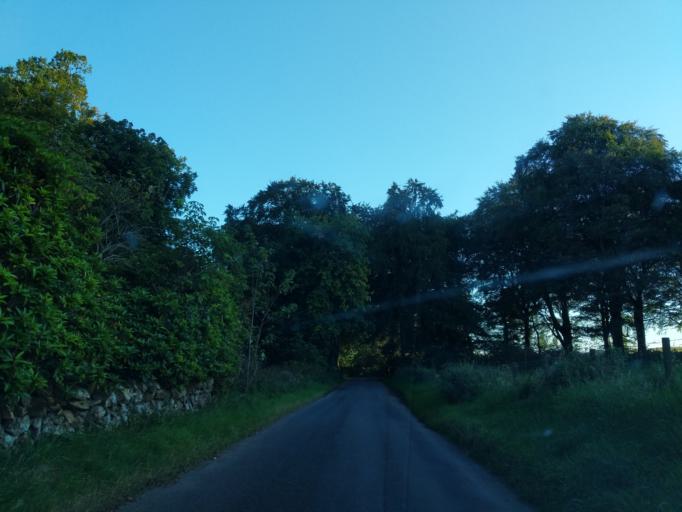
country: GB
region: Scotland
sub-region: The Scottish Borders
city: West Linton
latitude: 55.7068
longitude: -3.4357
